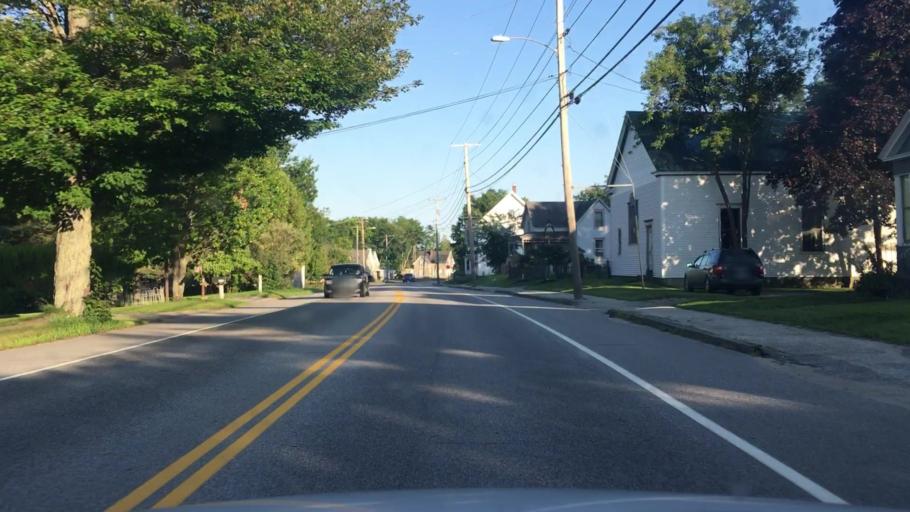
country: US
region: Maine
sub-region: Androscoggin County
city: Lisbon
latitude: 44.0205
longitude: -70.0949
